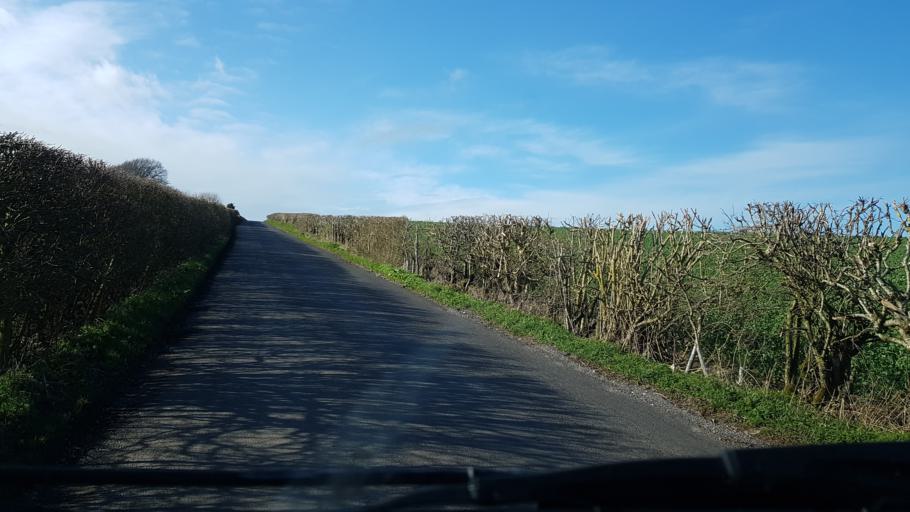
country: GB
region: England
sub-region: Wiltshire
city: Huish
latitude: 51.3959
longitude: -1.8120
